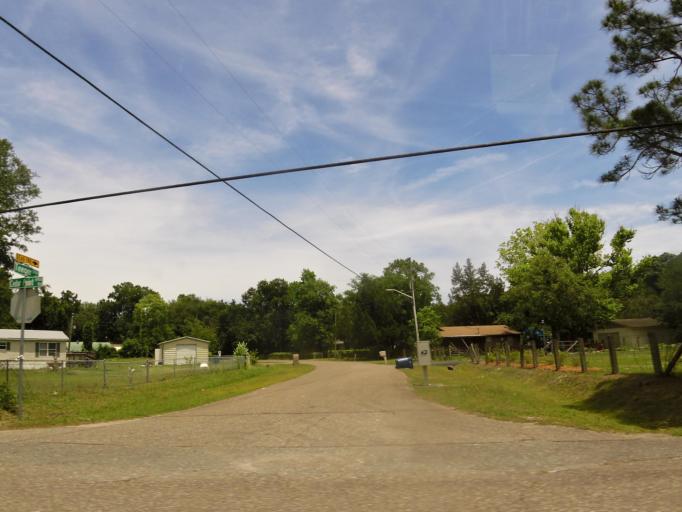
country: US
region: Florida
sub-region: Duval County
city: Jacksonville
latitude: 30.4599
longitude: -81.5355
